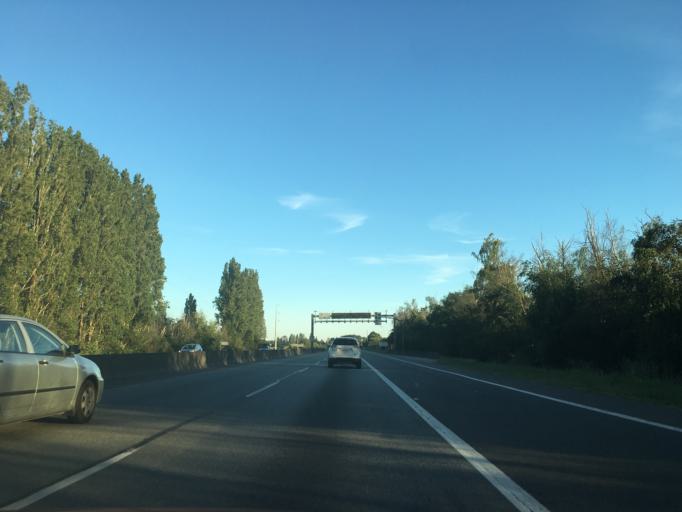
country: CA
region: British Columbia
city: Ladner
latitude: 49.1430
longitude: -123.0869
